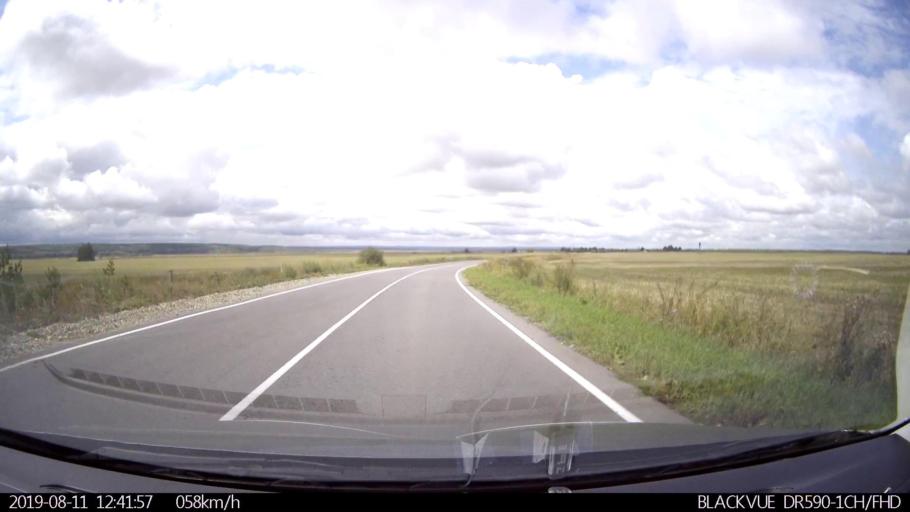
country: RU
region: Ulyanovsk
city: Ignatovka
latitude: 53.8425
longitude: 47.7574
